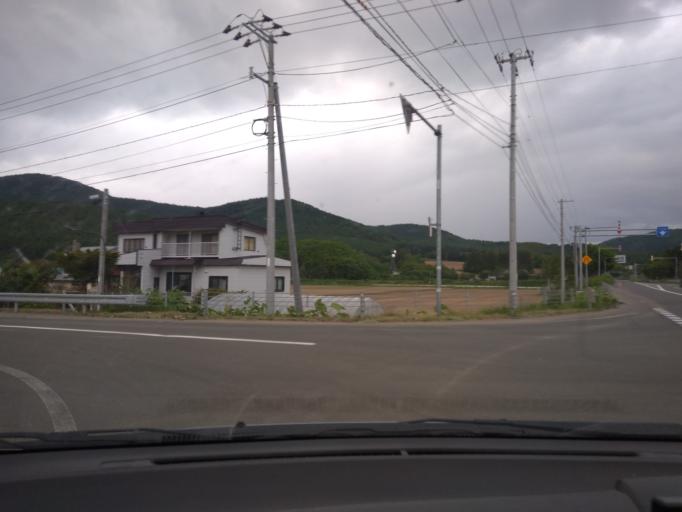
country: JP
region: Hokkaido
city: Shimo-furano
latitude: 43.1703
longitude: 142.5719
